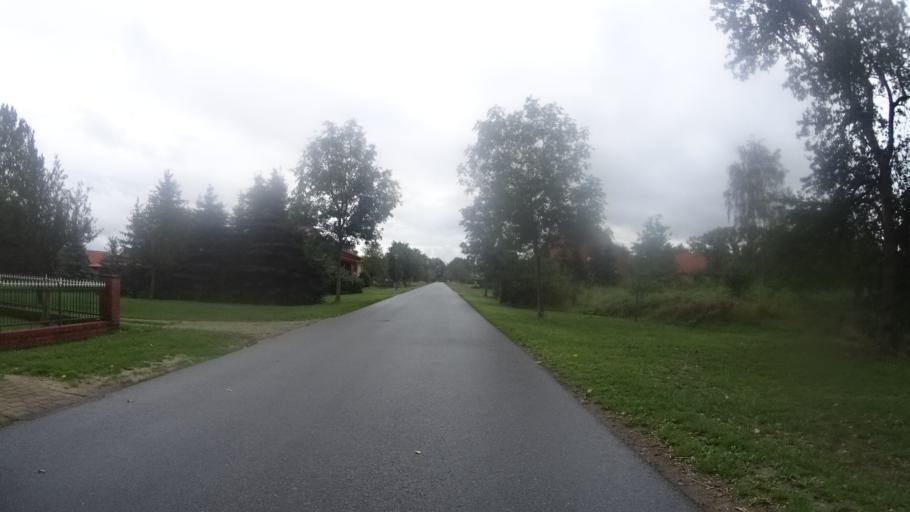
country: DE
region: Lower Saxony
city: Neu Darchau
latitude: 53.2428
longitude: 10.8901
